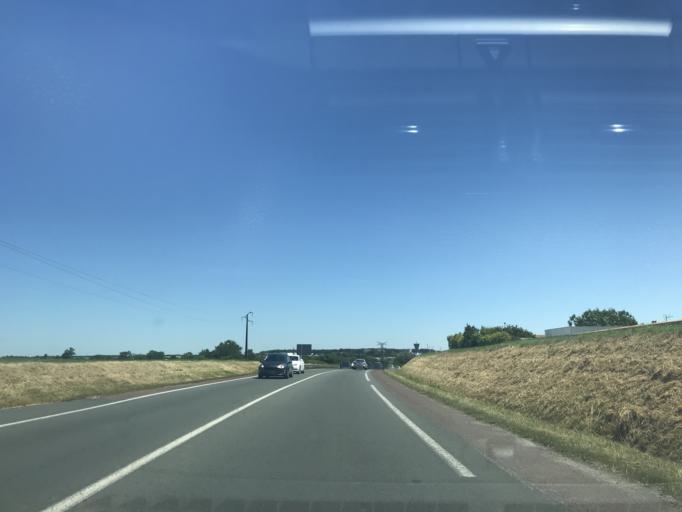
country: FR
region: Poitou-Charentes
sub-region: Departement de la Charente-Maritime
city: Royan
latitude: 45.6384
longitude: -1.0213
